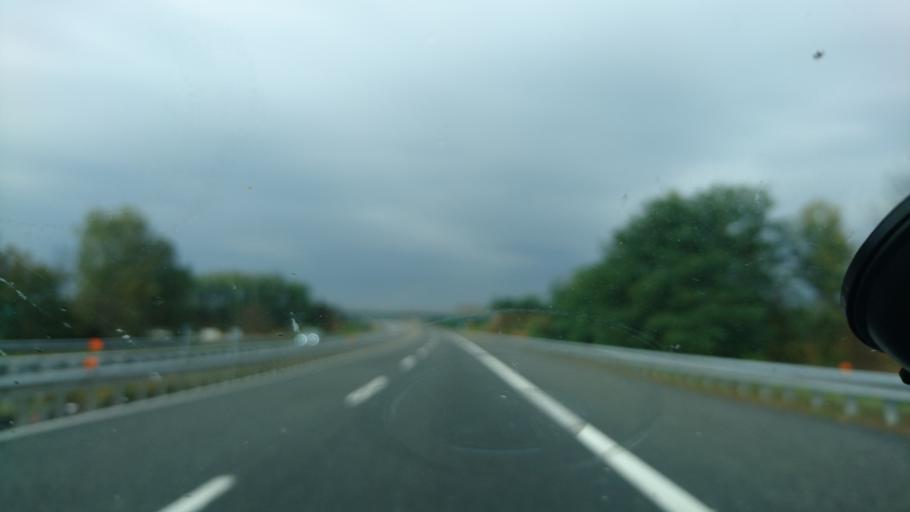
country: IT
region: Piedmont
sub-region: Provincia di Novara
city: Carpignano Sesia
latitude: 45.5322
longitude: 8.4316
